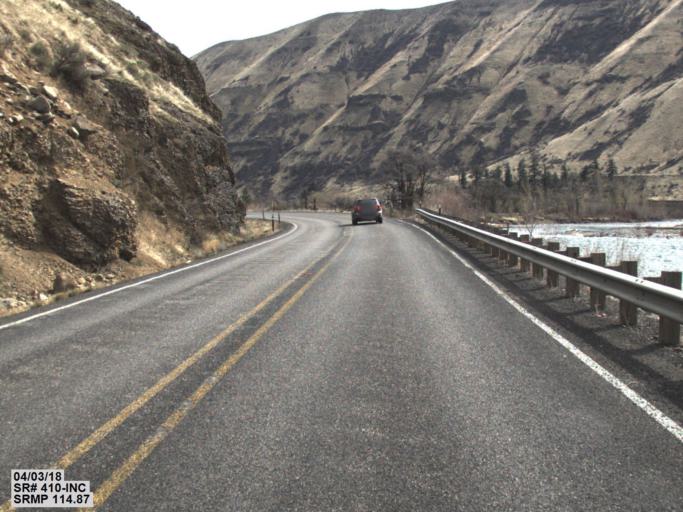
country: US
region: Washington
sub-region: Yakima County
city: Tieton
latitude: 46.7531
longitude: -120.8187
